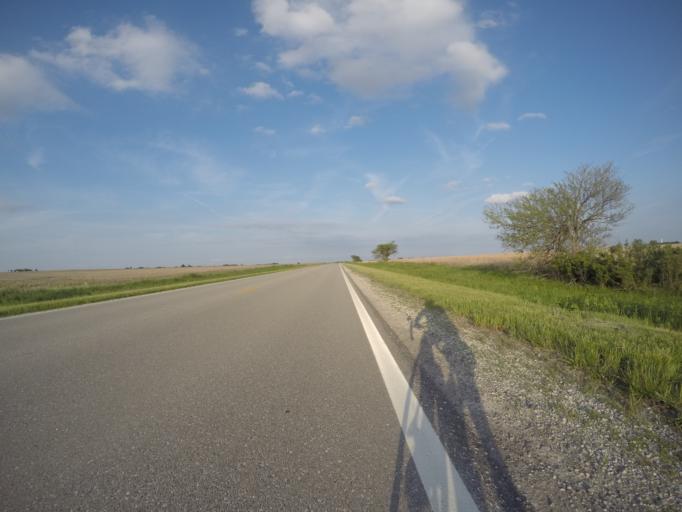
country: US
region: Kansas
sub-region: Pottawatomie County
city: Westmoreland
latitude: 39.4284
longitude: -96.5373
